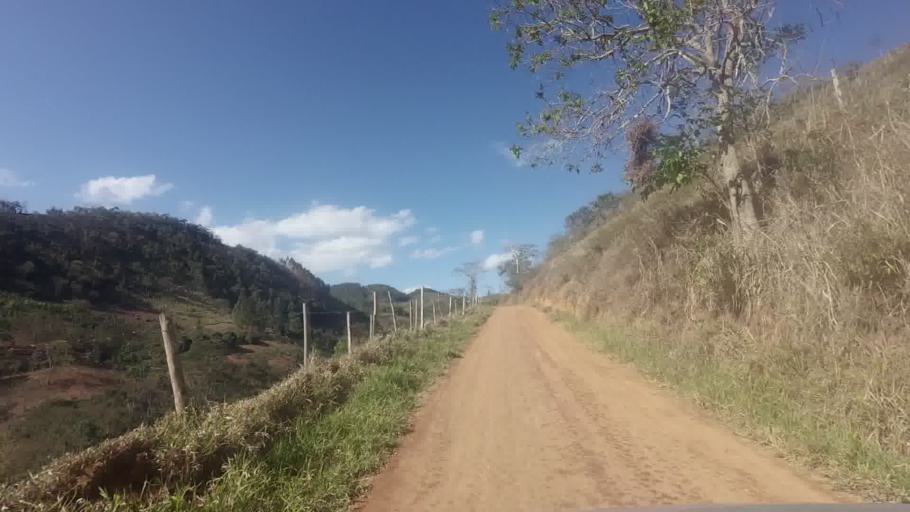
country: BR
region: Espirito Santo
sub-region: Sao Jose Do Calcado
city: Sao Jose do Calcado
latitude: -21.0303
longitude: -41.5844
